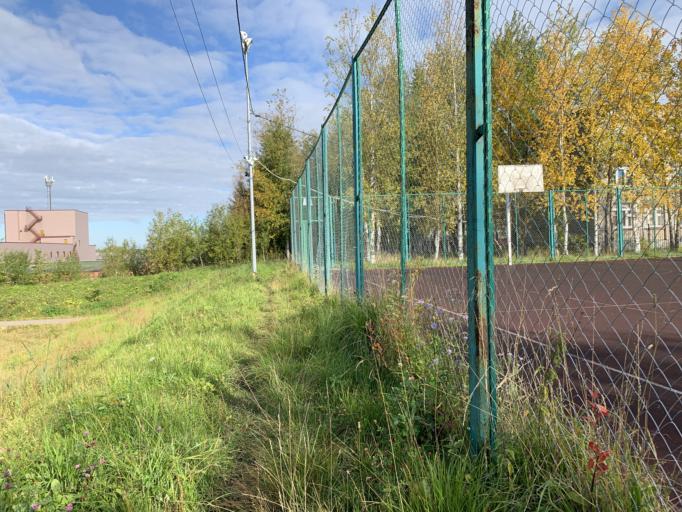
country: RU
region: Perm
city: Gubakha
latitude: 58.8359
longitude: 57.5593
